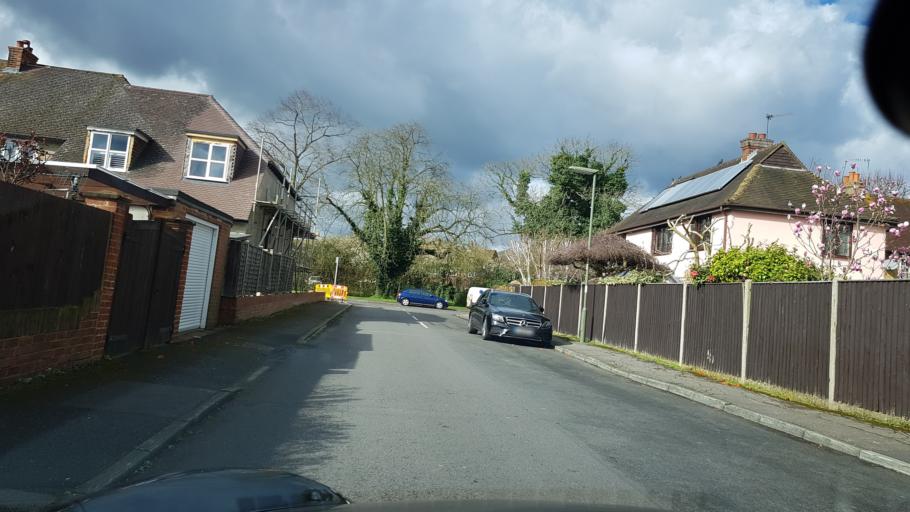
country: GB
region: England
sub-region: Surrey
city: Guildford
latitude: 51.2602
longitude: -0.5722
